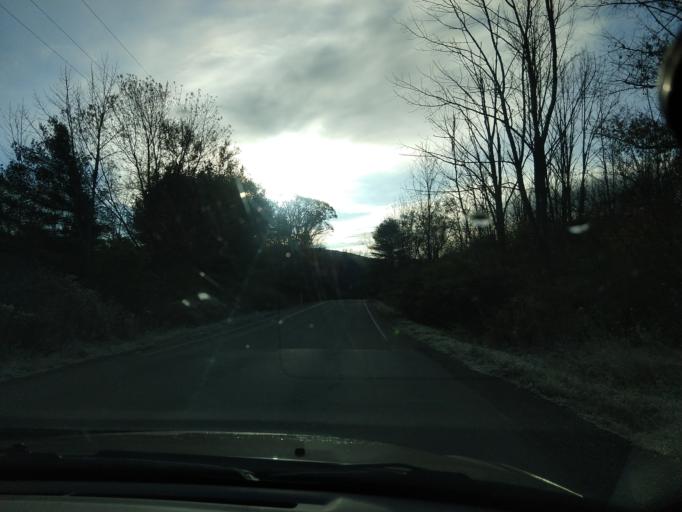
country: US
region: New York
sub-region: Tompkins County
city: Northeast Ithaca
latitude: 42.4602
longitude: -76.4433
